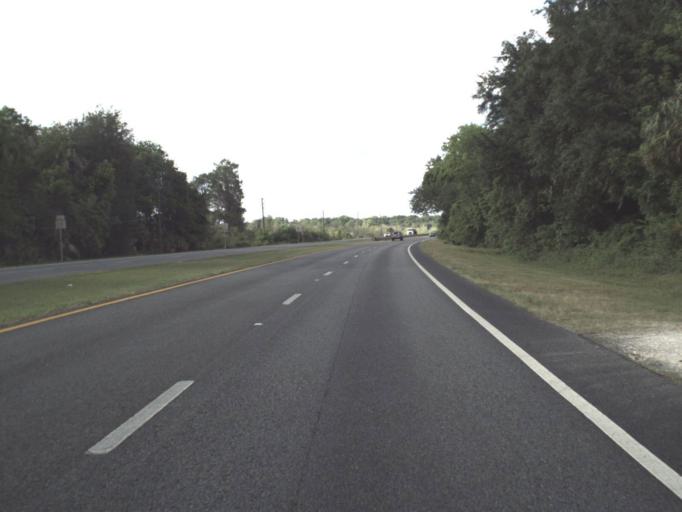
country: US
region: Florida
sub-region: Marion County
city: Citra
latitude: 29.4340
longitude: -82.1098
